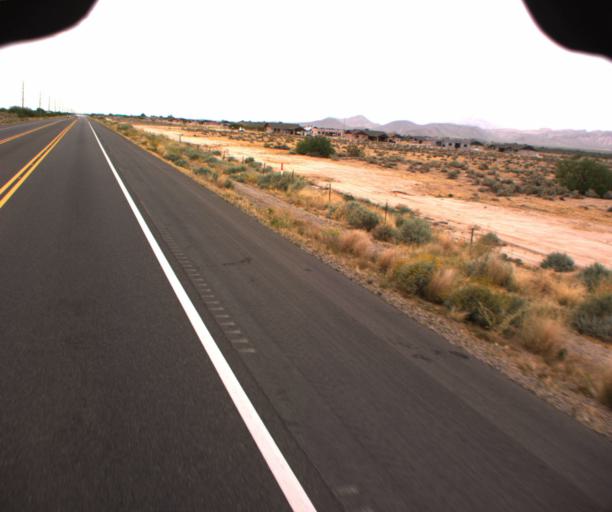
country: US
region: Arizona
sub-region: Pinal County
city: Sacaton
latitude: 33.0507
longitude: -111.6746
